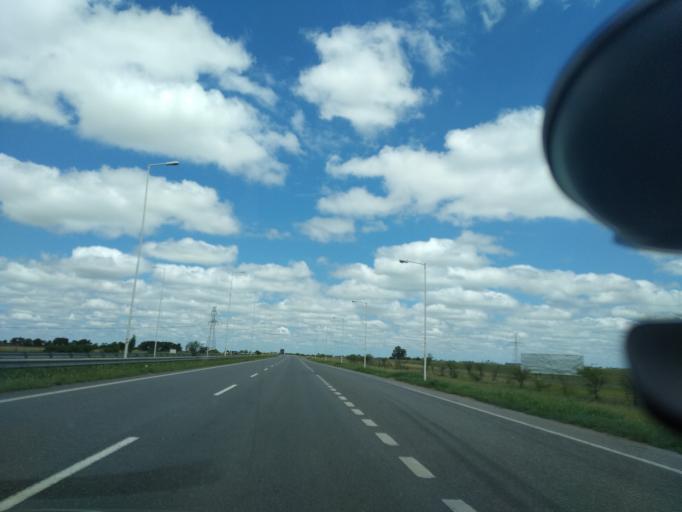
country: AR
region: Cordoba
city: Pilar
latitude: -31.6795
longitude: -63.8393
